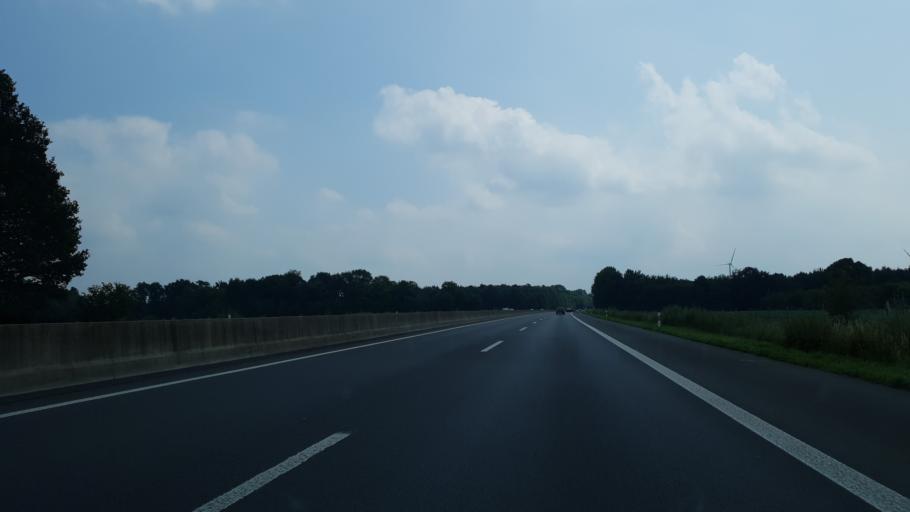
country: DE
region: North Rhine-Westphalia
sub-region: Regierungsbezirk Munster
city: Gescher
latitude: 51.9874
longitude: 7.0496
